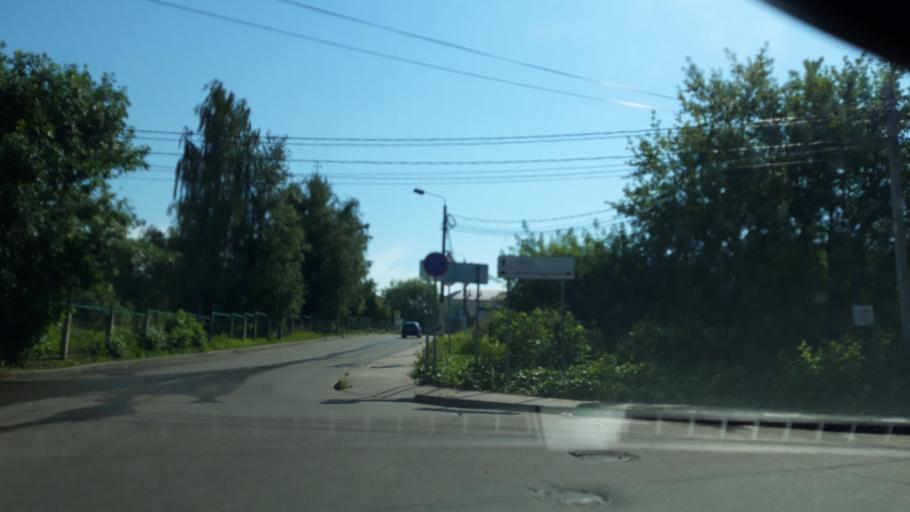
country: RU
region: Moskovskaya
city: Klin
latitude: 56.3322
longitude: 36.7331
